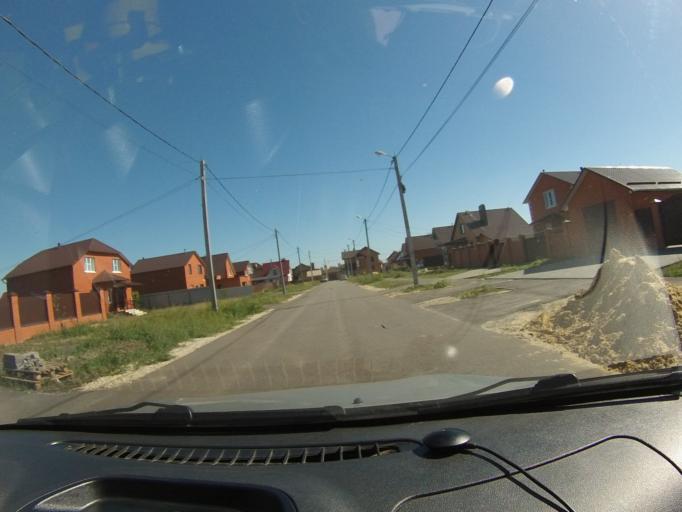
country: RU
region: Tambov
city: Tambov
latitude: 52.7706
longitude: 41.3738
